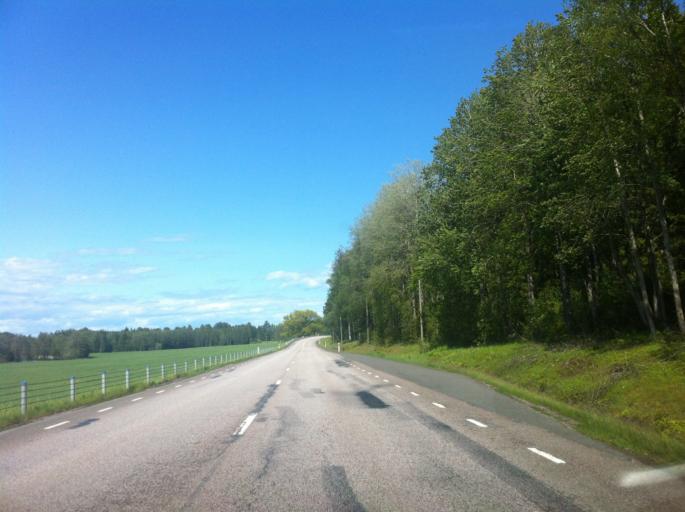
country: SE
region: Vaestra Goetaland
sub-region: Gullspangs Kommun
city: Gullspang
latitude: 59.0053
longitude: 14.1037
